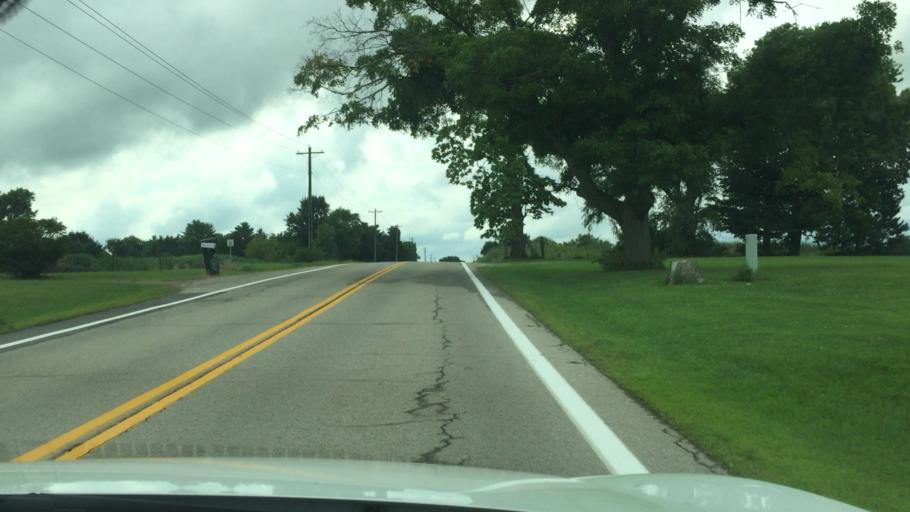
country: US
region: Ohio
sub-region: Champaign County
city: Mechanicsburg
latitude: 40.0889
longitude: -83.6025
